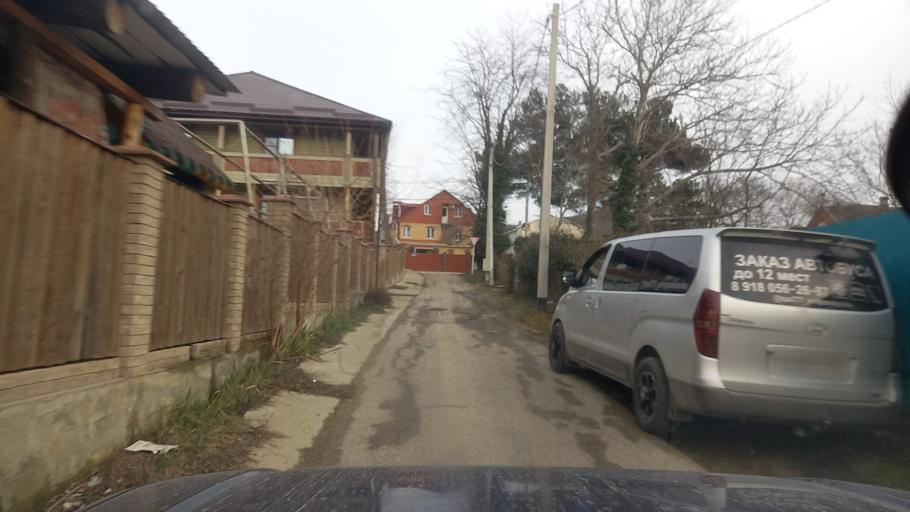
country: RU
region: Krasnodarskiy
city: Arkhipo-Osipovka
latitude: 44.3668
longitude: 38.5349
